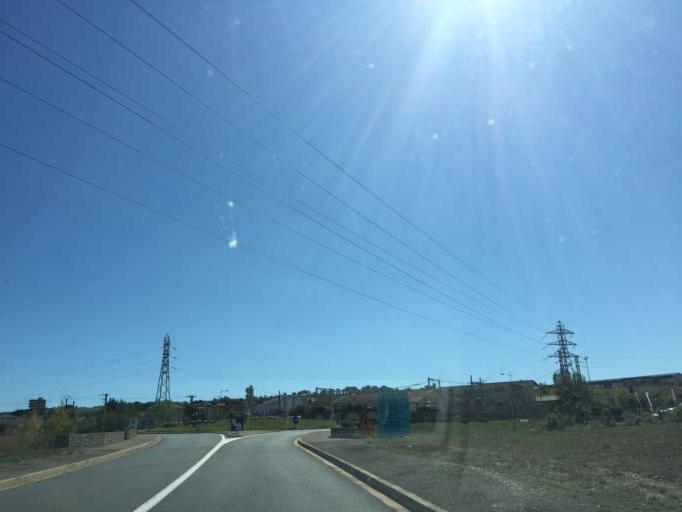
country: FR
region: Midi-Pyrenees
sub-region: Departement de l'Aveyron
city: Saint-Affrique
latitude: 43.9765
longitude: 2.9623
